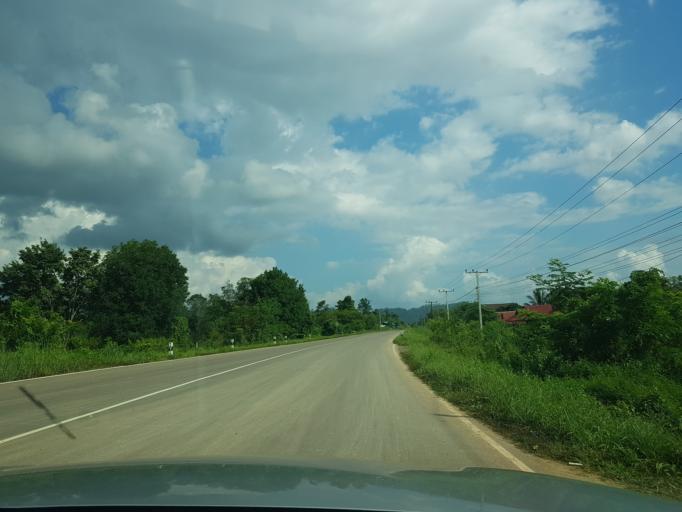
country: TH
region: Nong Khai
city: Sangkhom
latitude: 18.1525
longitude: 102.2017
